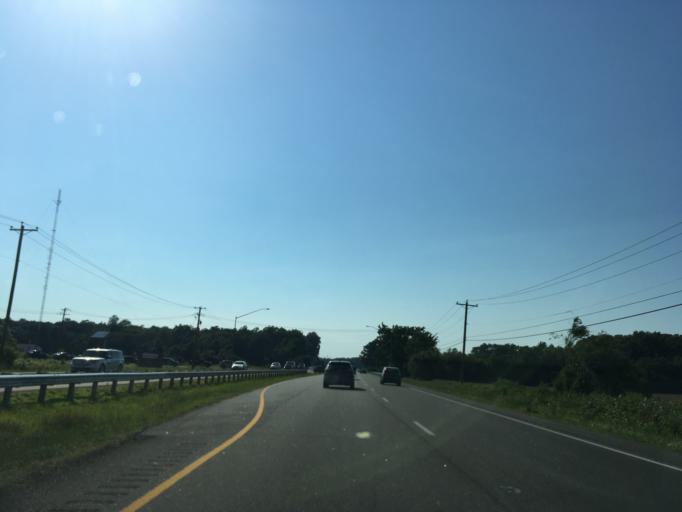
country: US
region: Maryland
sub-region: Queen Anne's County
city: Centreville
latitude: 38.9584
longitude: -76.0917
